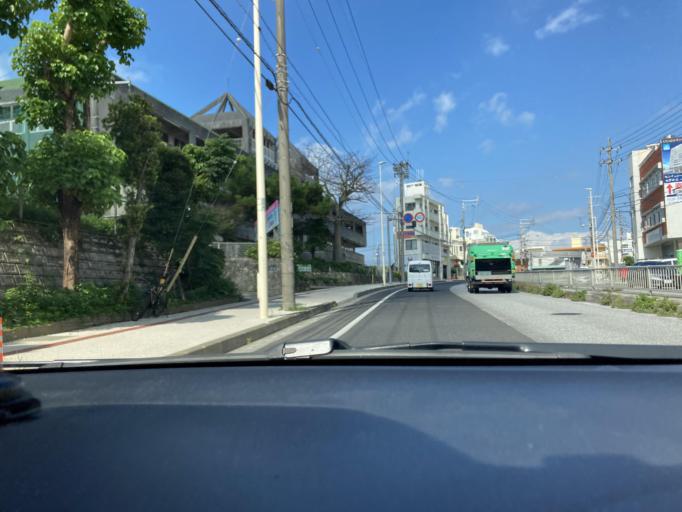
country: JP
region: Okinawa
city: Naha-shi
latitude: 26.2361
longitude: 127.6984
